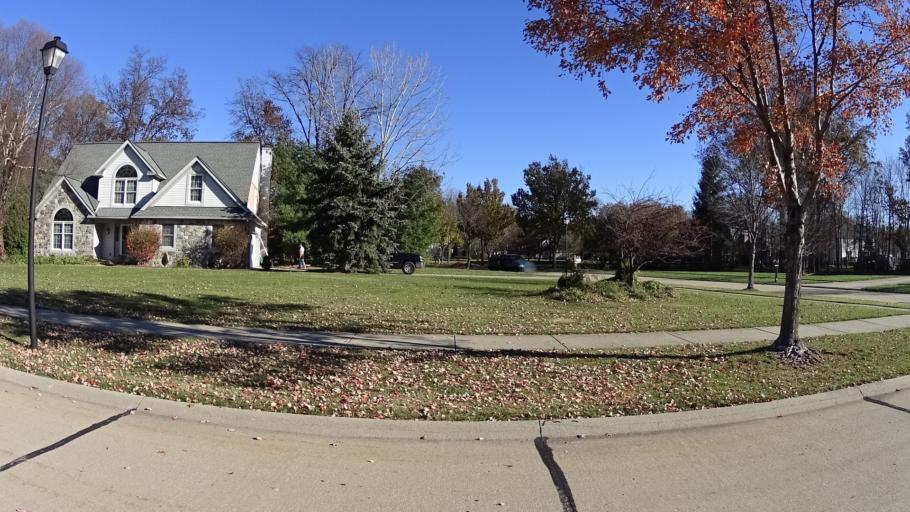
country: US
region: Ohio
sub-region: Lorain County
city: Avon Lake
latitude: 41.4989
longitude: -82.0080
